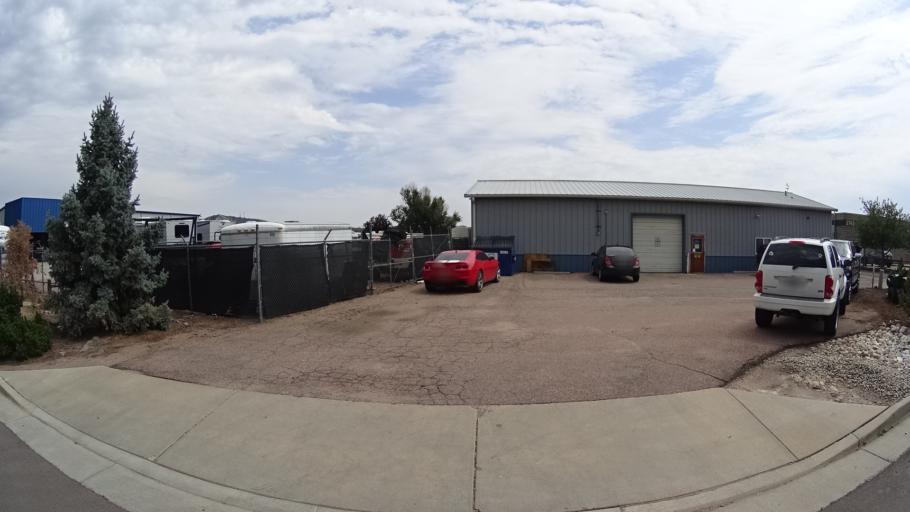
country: US
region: Colorado
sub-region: El Paso County
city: Colorado Springs
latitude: 38.8858
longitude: -104.8310
